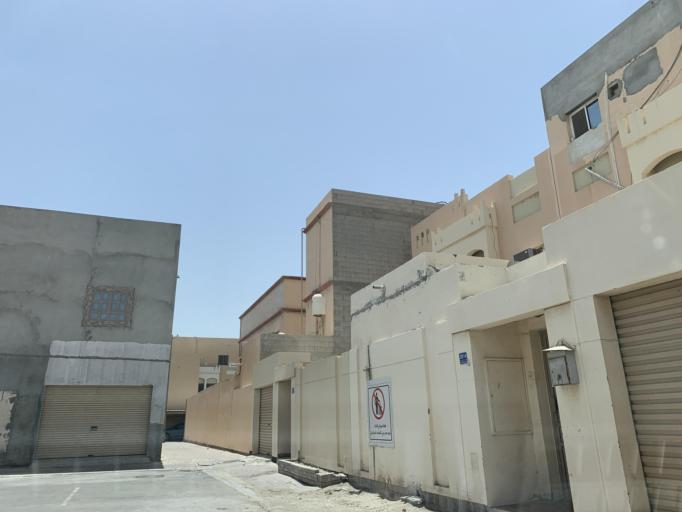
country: BH
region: Northern
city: Sitrah
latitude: 26.1401
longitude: 50.5916
